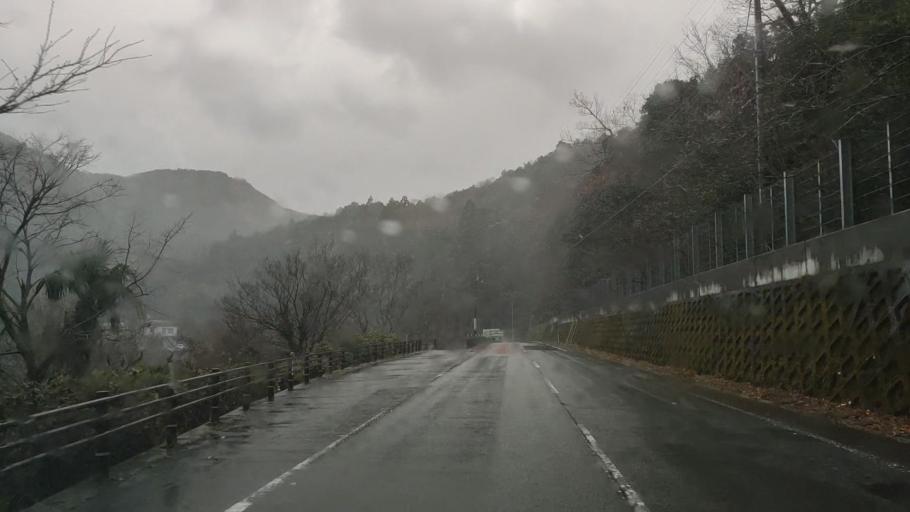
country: JP
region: Tokushima
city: Kamojimacho-jogejima
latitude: 34.1493
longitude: 134.3529
